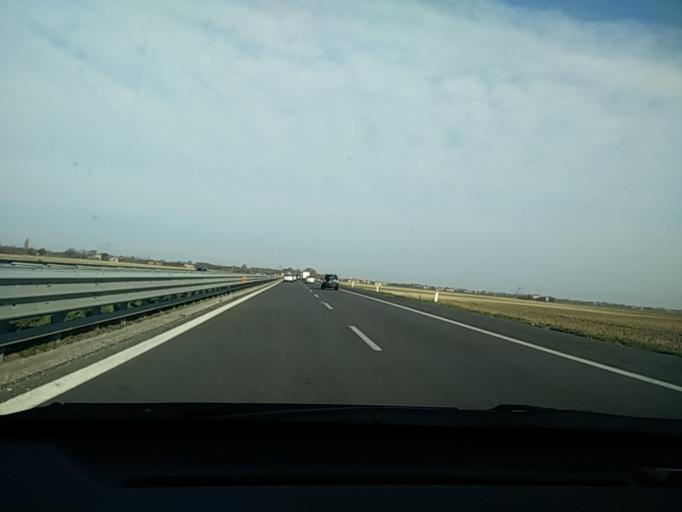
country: IT
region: Veneto
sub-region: Provincia di Venezia
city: Tessera
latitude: 45.5199
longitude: 12.3317
